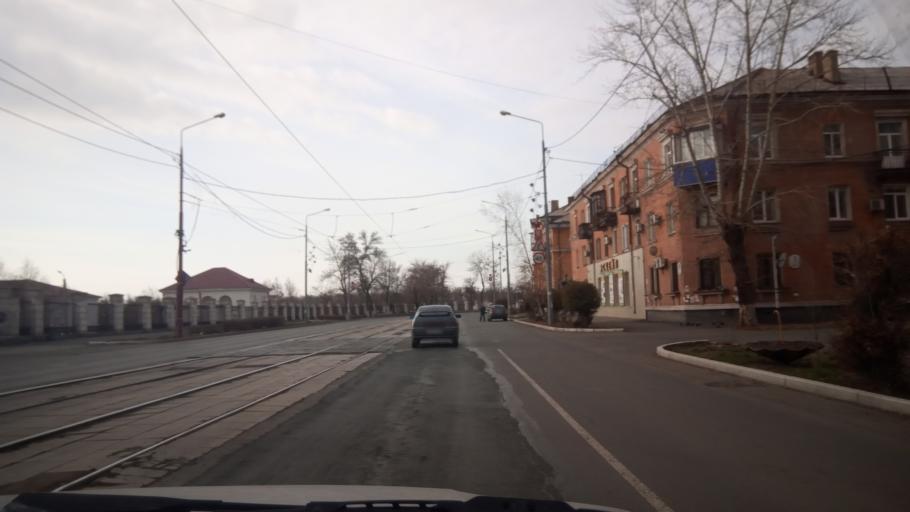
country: RU
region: Orenburg
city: Novotroitsk
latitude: 51.1968
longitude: 58.3306
